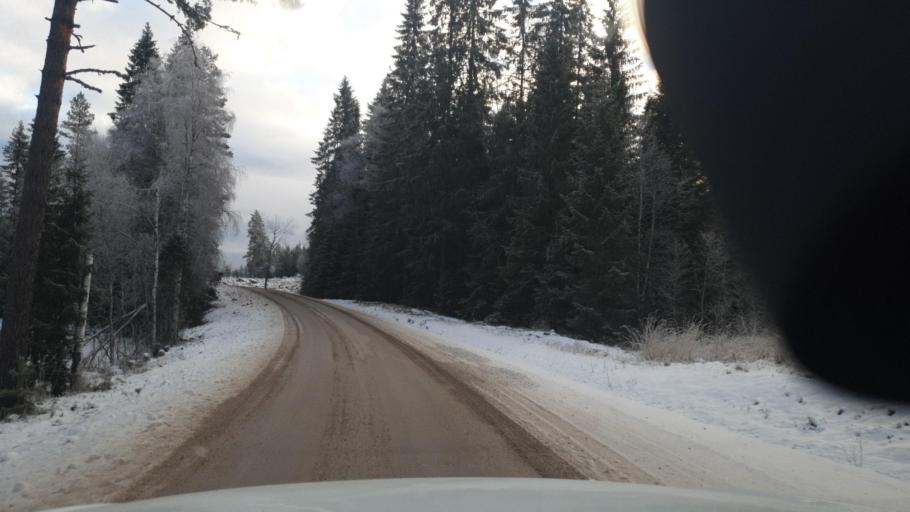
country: SE
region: Vaermland
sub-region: Eda Kommun
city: Charlottenberg
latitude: 60.0476
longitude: 12.5723
